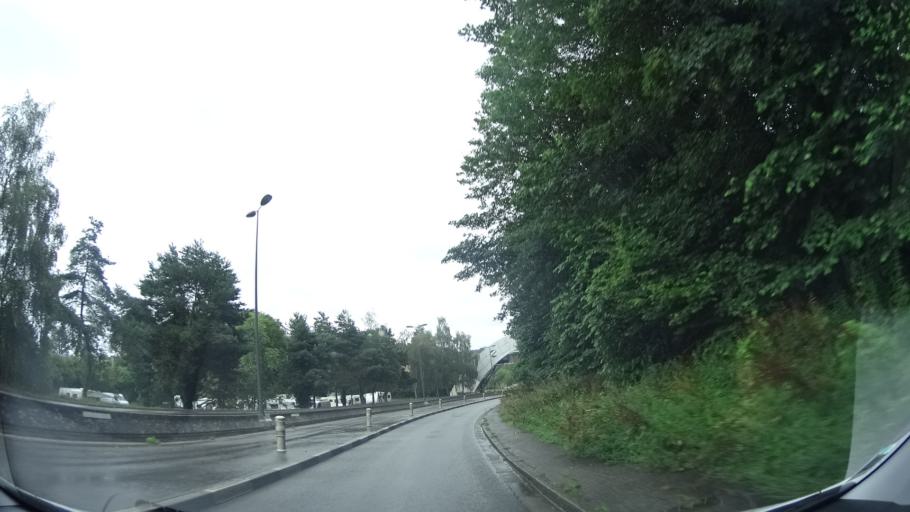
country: FR
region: Lower Normandy
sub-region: Departement de la Manche
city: Octeville
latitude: 49.6297
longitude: -1.6309
